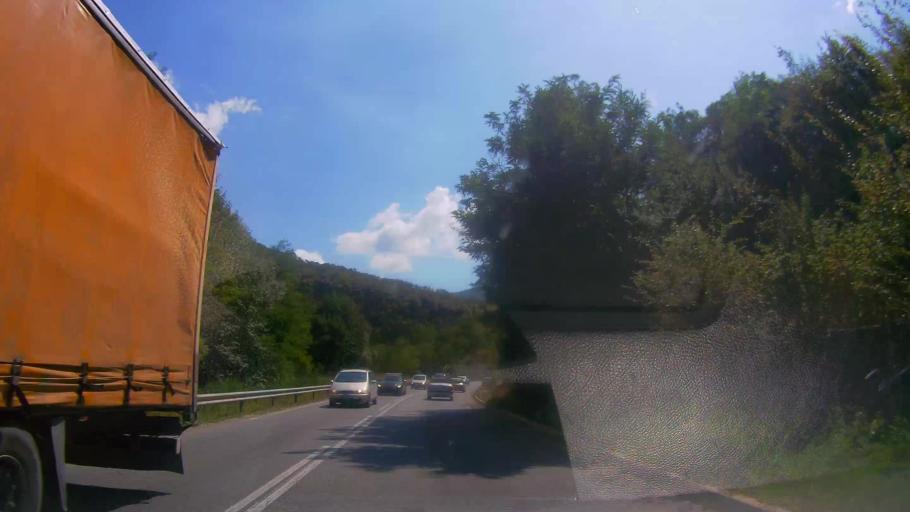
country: BG
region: Stara Zagora
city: Gurkovo
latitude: 42.7151
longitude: 25.7179
